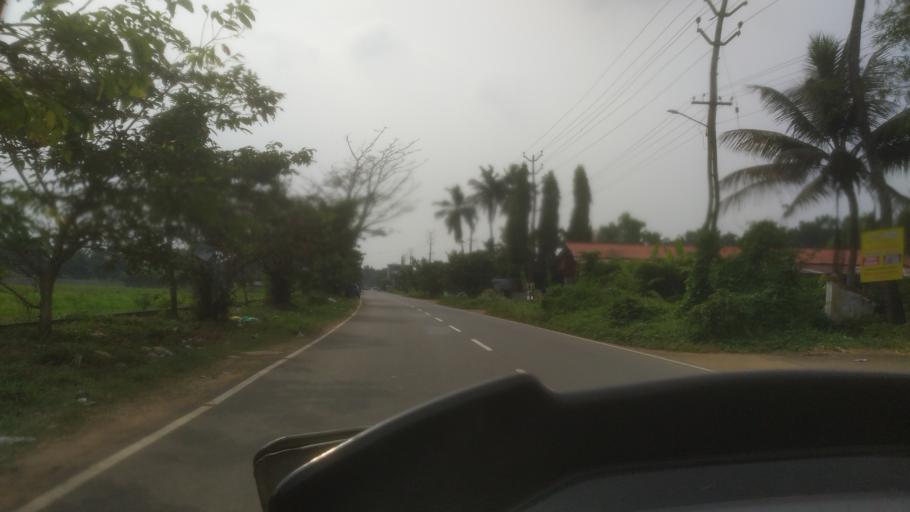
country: IN
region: Kerala
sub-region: Ernakulam
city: Angamali
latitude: 10.1639
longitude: 76.4019
